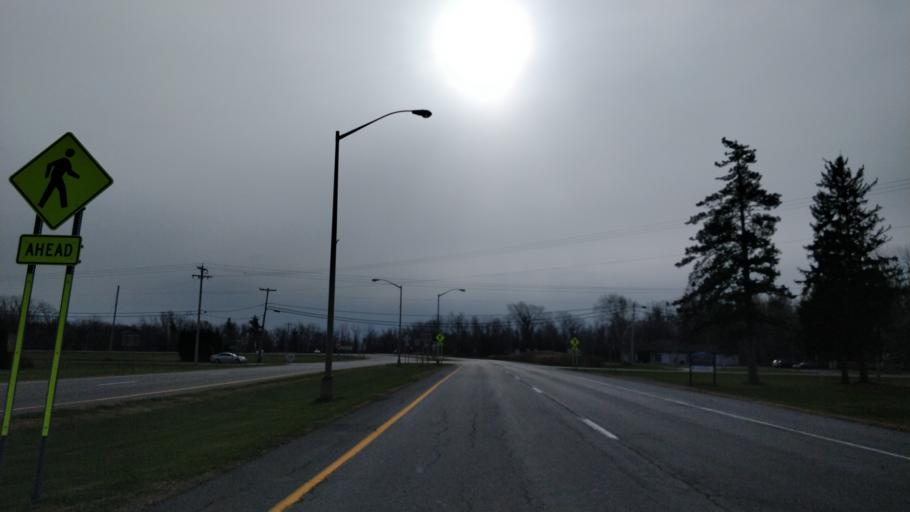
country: US
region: New York
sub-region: St. Lawrence County
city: Ogdensburg
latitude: 44.7163
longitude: -75.4528
